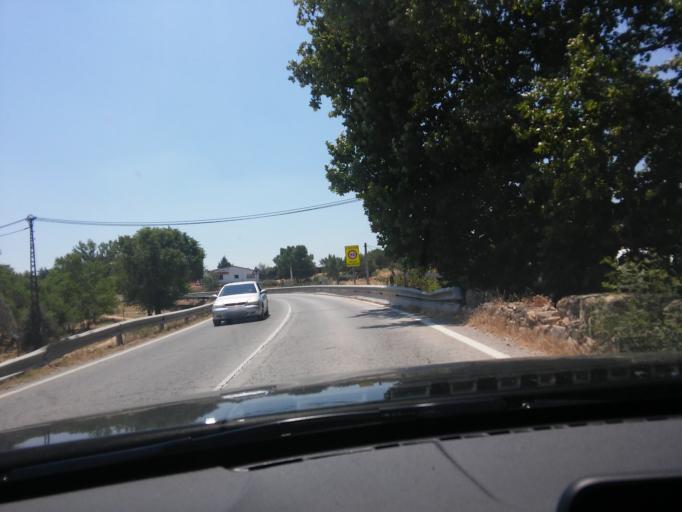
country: ES
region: Madrid
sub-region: Provincia de Madrid
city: Collado-Villalba
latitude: 40.6288
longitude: -4.0299
